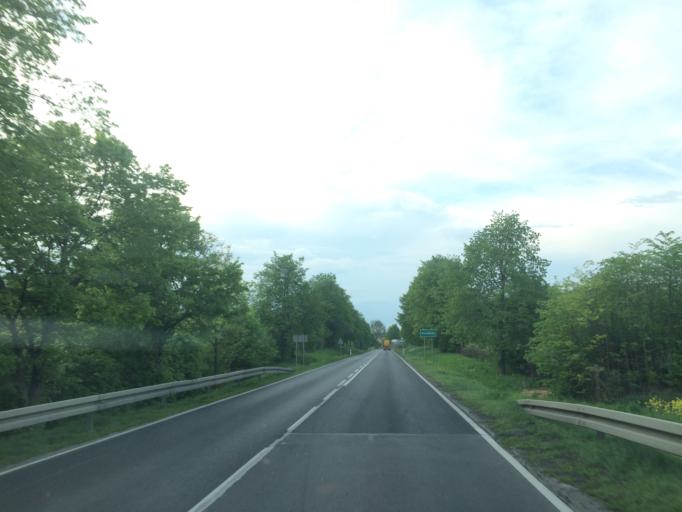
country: PL
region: Warmian-Masurian Voivodeship
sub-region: Powiat nowomiejski
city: Kurzetnik
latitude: 53.3862
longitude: 19.5720
